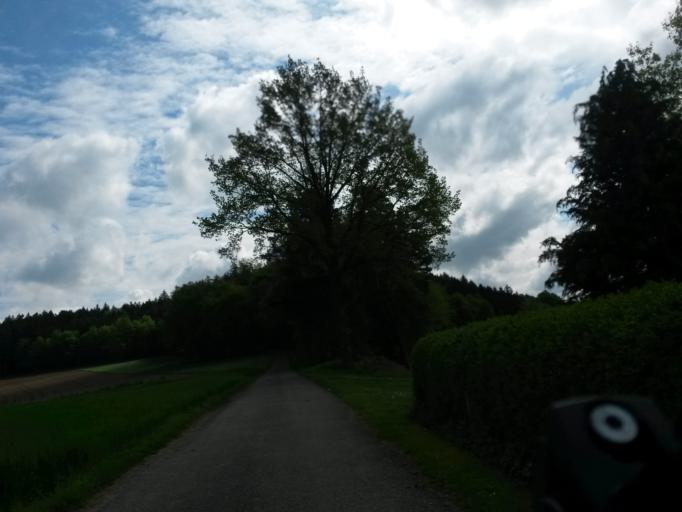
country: DE
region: Baden-Wuerttemberg
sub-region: Tuebingen Region
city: Bad Waldsee
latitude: 47.8973
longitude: 9.7278
